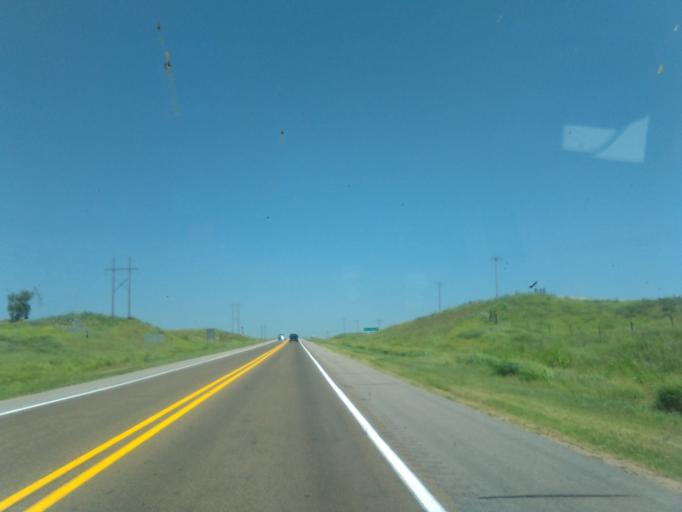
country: US
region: Nebraska
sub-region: Lincoln County
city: North Platte
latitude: 40.8283
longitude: -100.7537
